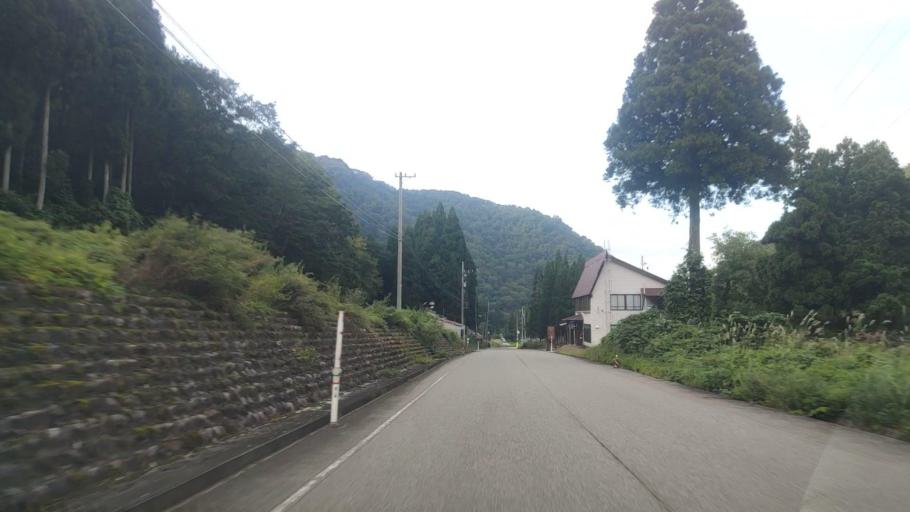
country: JP
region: Toyama
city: Yatsuomachi-higashikumisaka
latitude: 36.4353
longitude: 137.0815
